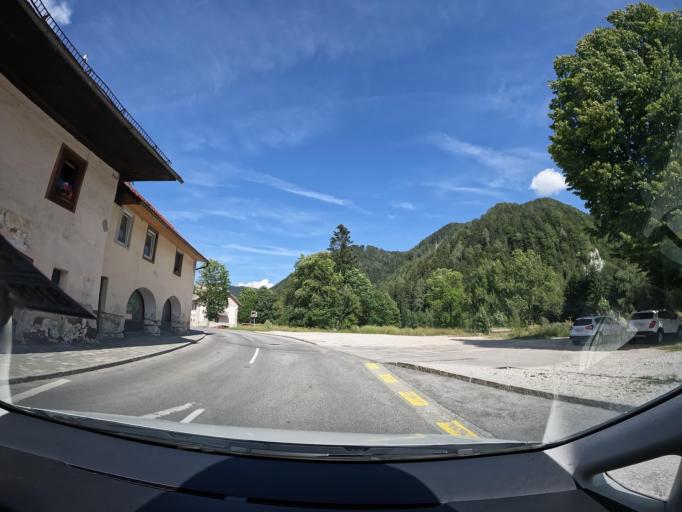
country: AT
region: Carinthia
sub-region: Politischer Bezirk Klagenfurt Land
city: Moosburg
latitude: 46.6744
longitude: 14.1244
